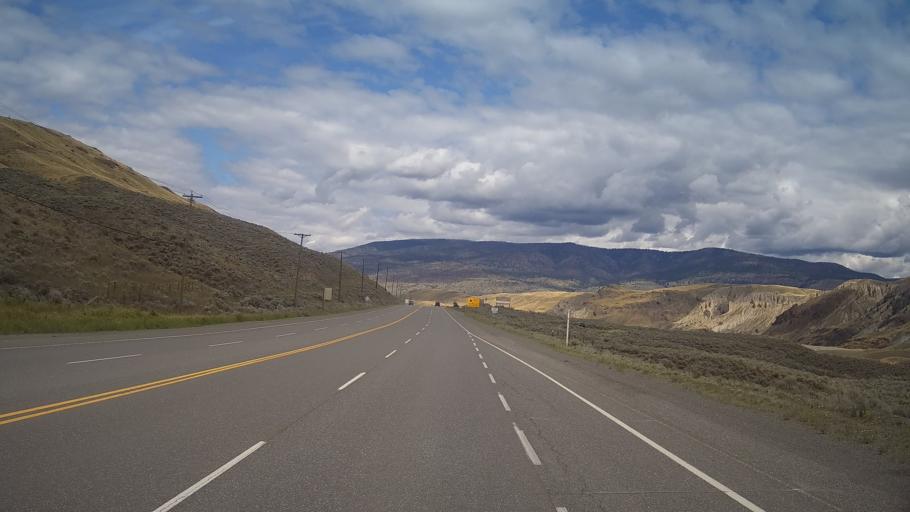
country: CA
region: British Columbia
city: Cache Creek
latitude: 50.7749
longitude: -121.3130
